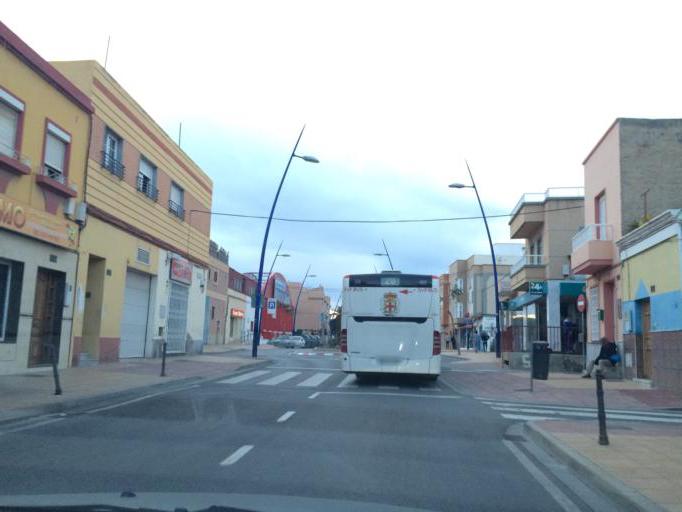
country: ES
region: Andalusia
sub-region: Provincia de Almeria
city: Almeria
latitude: 36.8410
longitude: -2.4107
